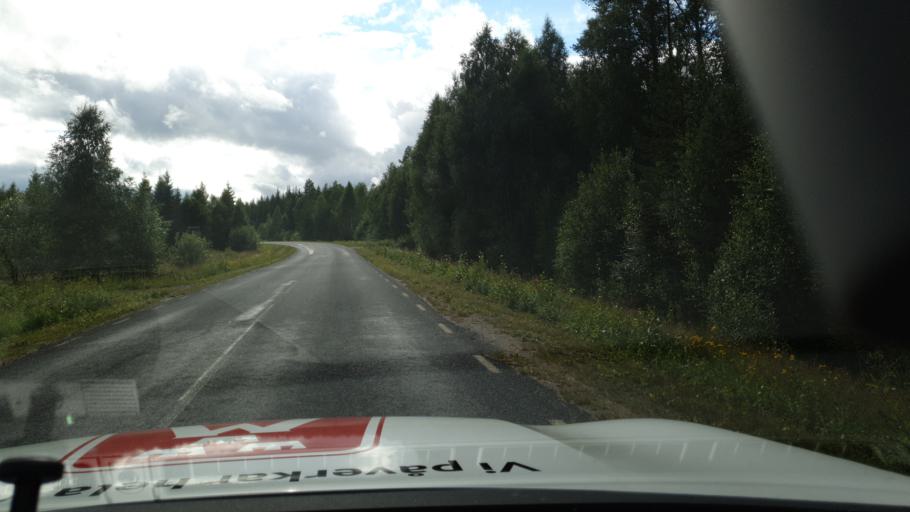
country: SE
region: Vaesterbotten
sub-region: Skelleftea Kommun
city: Soedra Bergsbyn
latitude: 64.5929
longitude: 21.0552
